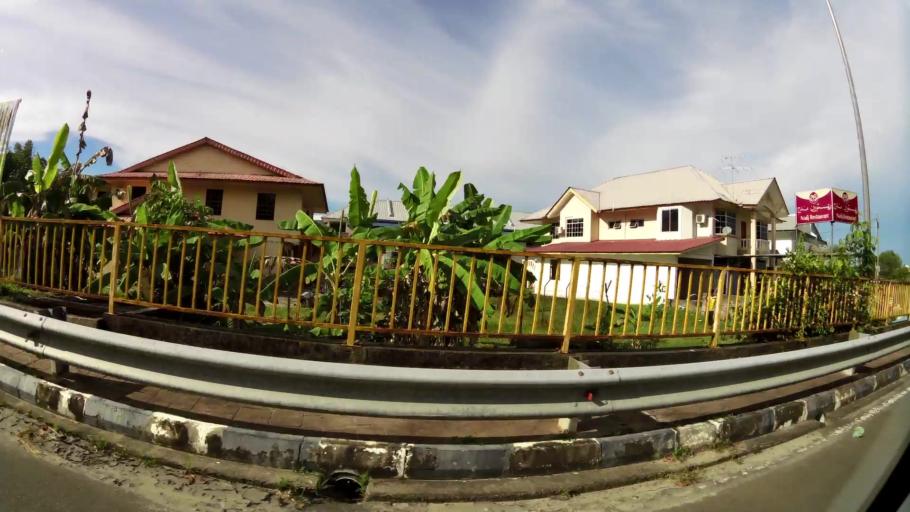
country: BN
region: Brunei and Muara
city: Bandar Seri Begawan
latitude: 4.9704
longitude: 115.0212
